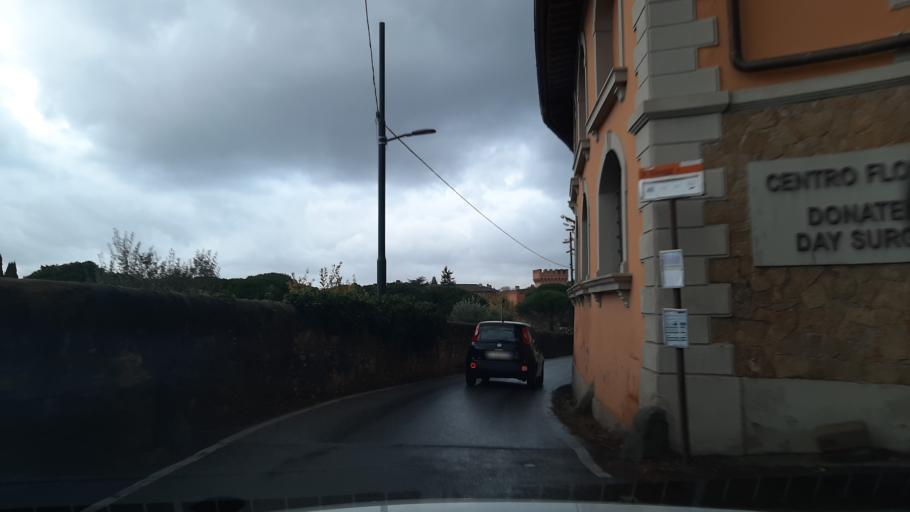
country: IT
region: Tuscany
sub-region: Province of Florence
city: Florence
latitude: 43.8117
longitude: 11.2533
